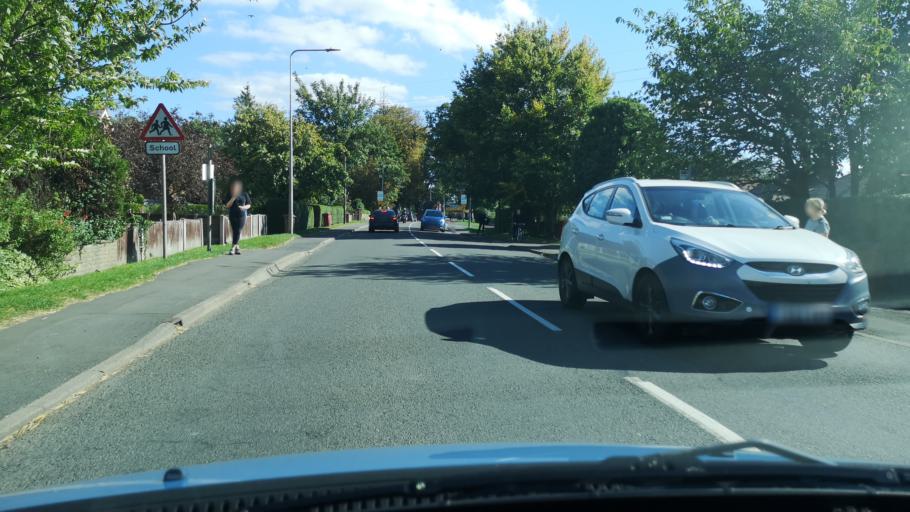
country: GB
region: England
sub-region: North Lincolnshire
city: Crowle
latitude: 53.6015
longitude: -0.8285
